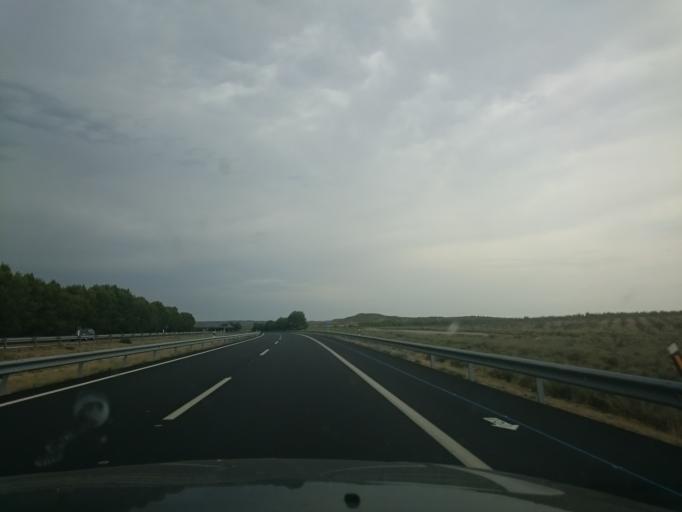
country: ES
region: Aragon
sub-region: Provincia de Zaragoza
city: Pina de Ebro
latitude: 41.5423
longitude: -0.5361
